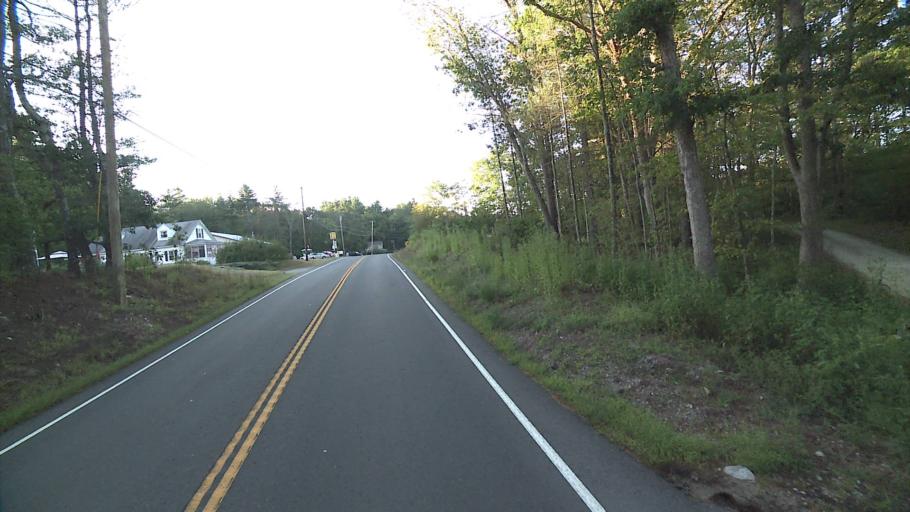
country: US
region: Connecticut
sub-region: Tolland County
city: Stafford
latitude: 41.9969
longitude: -72.3162
